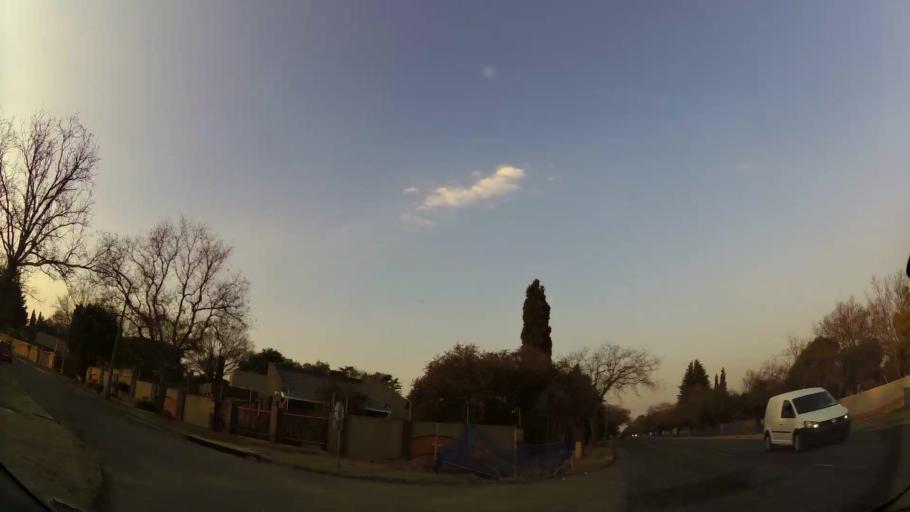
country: ZA
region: Gauteng
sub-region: Ekurhuleni Metropolitan Municipality
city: Benoni
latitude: -26.1734
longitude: 28.3361
